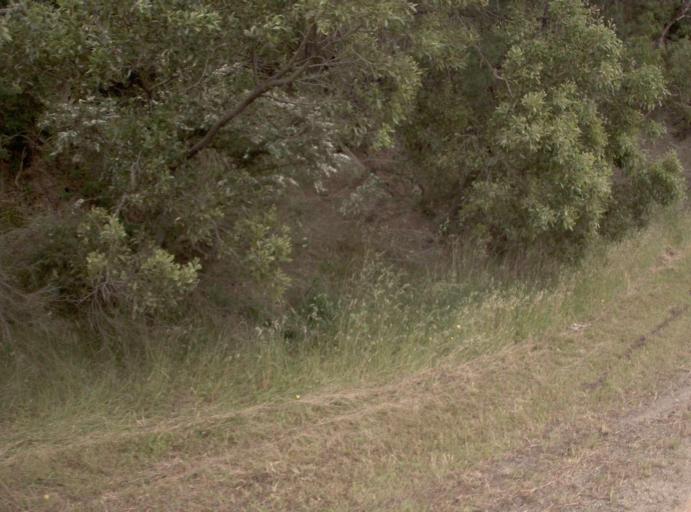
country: AU
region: Victoria
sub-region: Wellington
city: Sale
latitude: -38.1726
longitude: 147.0198
